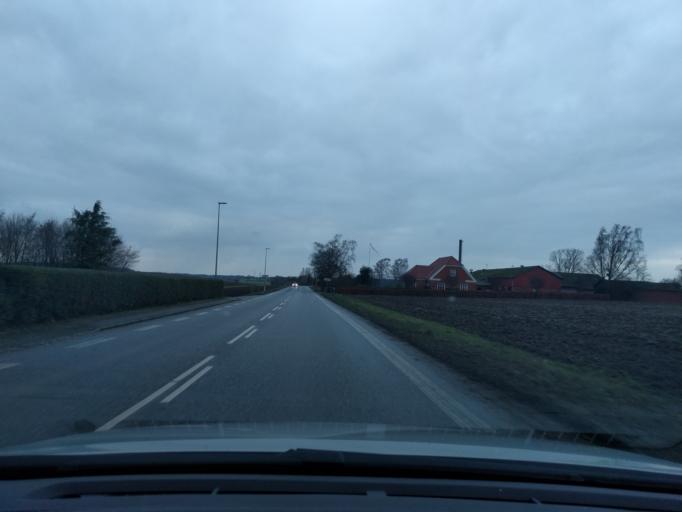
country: DK
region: Zealand
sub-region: Guldborgsund Kommune
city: Stubbekobing
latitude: 54.8062
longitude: 11.9944
